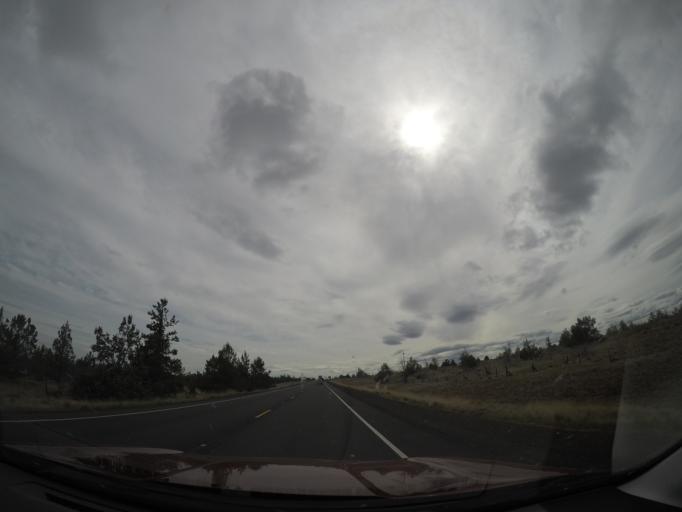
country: US
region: Oregon
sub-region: Jefferson County
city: Madras
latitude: 44.9277
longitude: -120.9393
